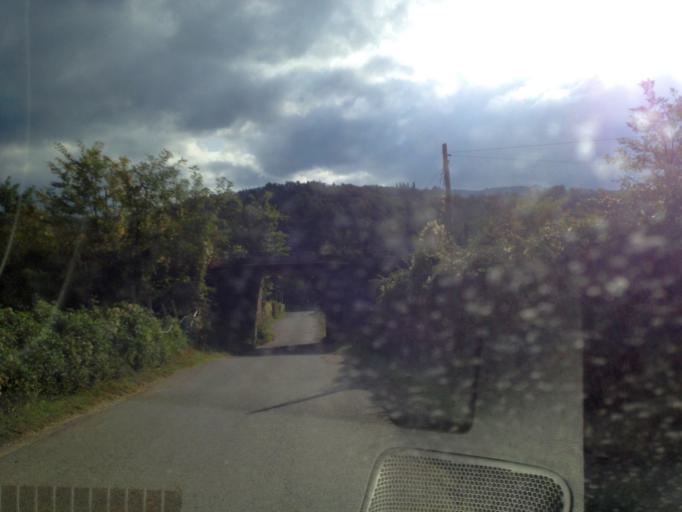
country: IT
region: Tuscany
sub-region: Province of Florence
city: Montebonello
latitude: 43.8507
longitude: 11.5040
